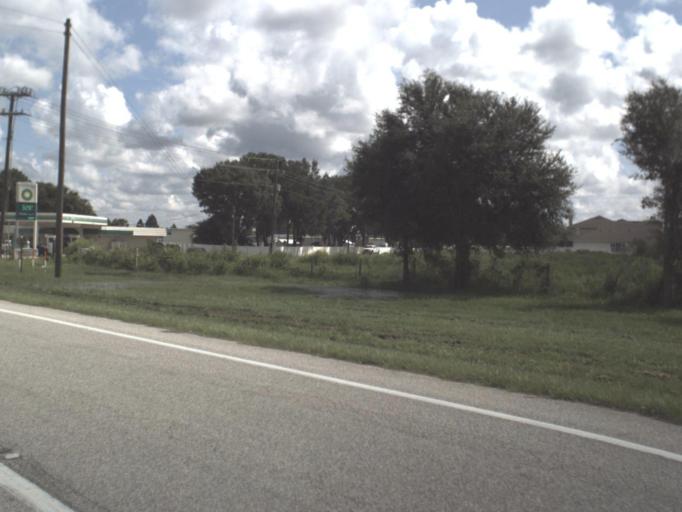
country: US
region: Florida
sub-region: Polk County
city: Polk City
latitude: 28.1609
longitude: -81.8586
